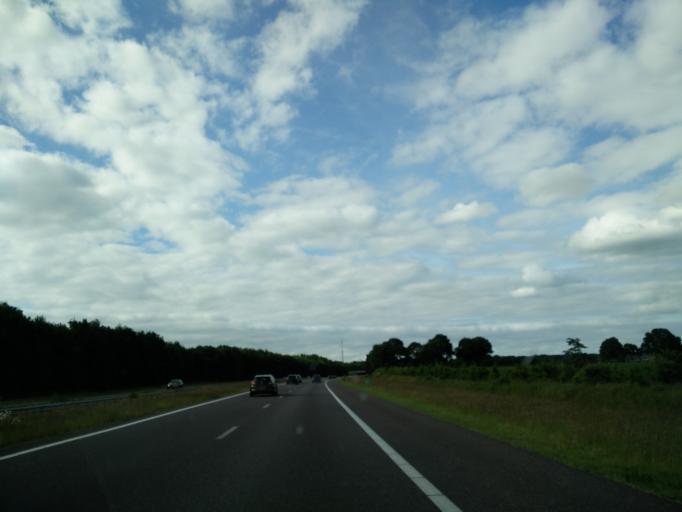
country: NL
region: Drenthe
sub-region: Gemeente Assen
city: Assen
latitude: 52.9129
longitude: 6.5312
